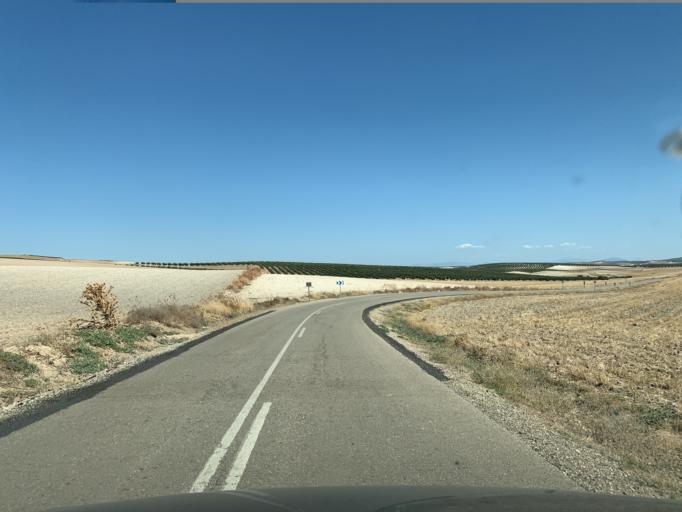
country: ES
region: Andalusia
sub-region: Provincia de Sevilla
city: El Rubio
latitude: 37.3498
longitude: -5.0453
